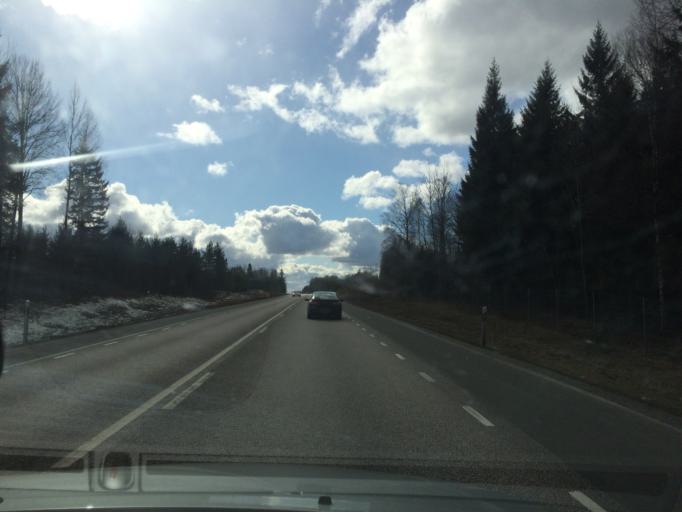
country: SE
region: Vaestra Goetaland
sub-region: Gotene Kommun
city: Goetene
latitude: 58.5902
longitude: 13.6240
